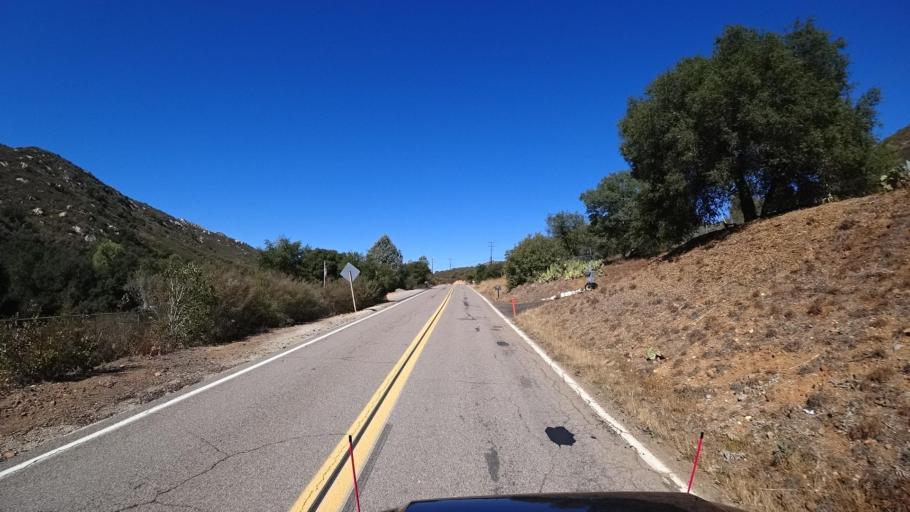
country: US
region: California
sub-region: San Diego County
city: Alpine
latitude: 32.7059
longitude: -116.7329
